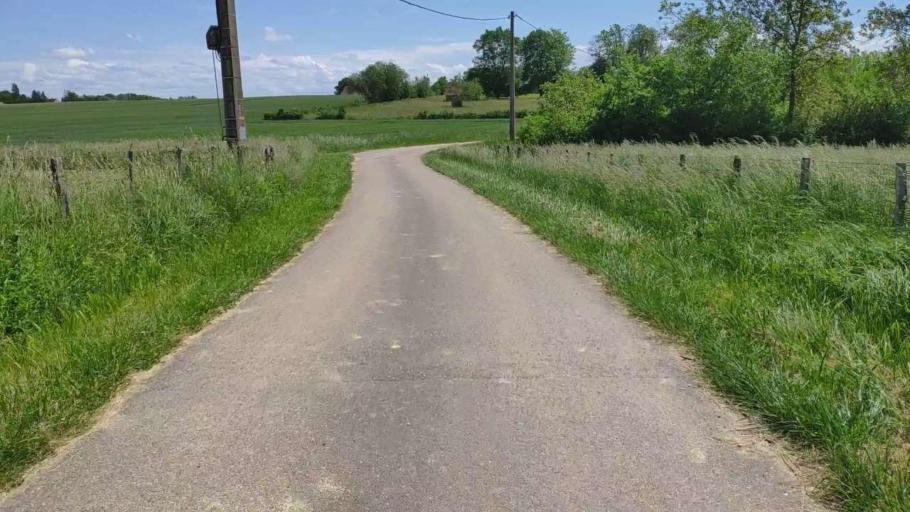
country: FR
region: Franche-Comte
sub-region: Departement du Jura
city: Bletterans
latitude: 46.8003
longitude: 5.3910
